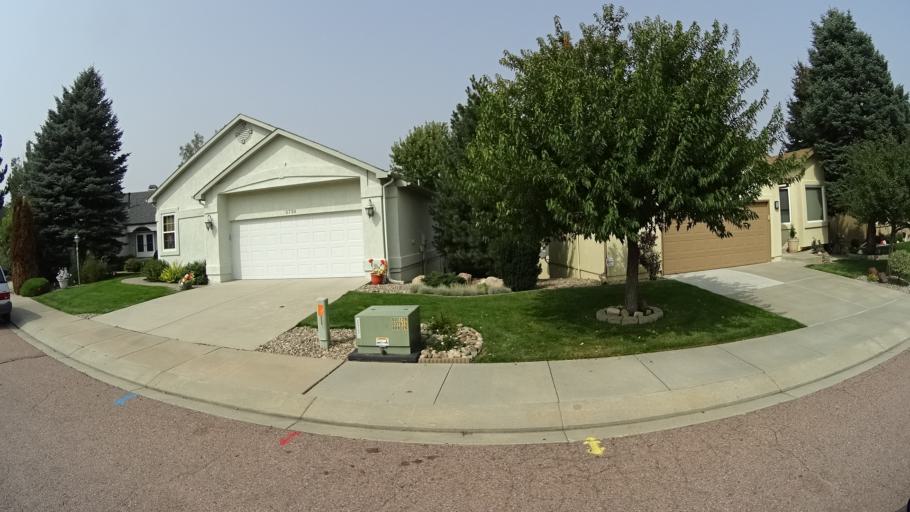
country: US
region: Colorado
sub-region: El Paso County
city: Cimarron Hills
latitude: 38.9207
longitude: -104.7443
